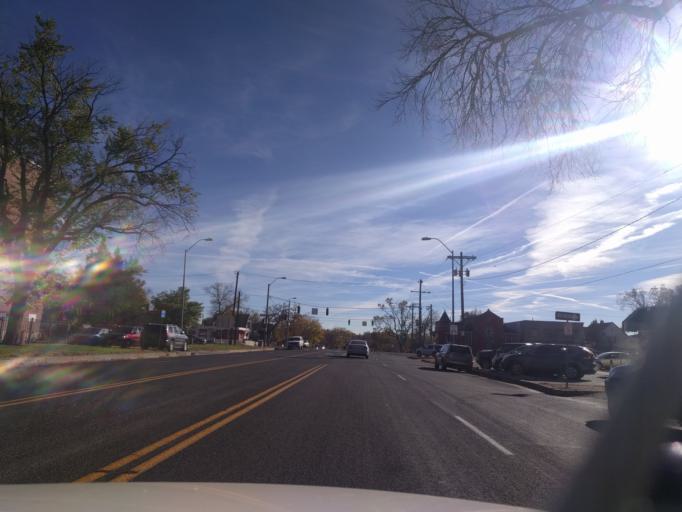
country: US
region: Colorado
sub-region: El Paso County
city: Colorado Springs
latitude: 38.8380
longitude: -104.8208
